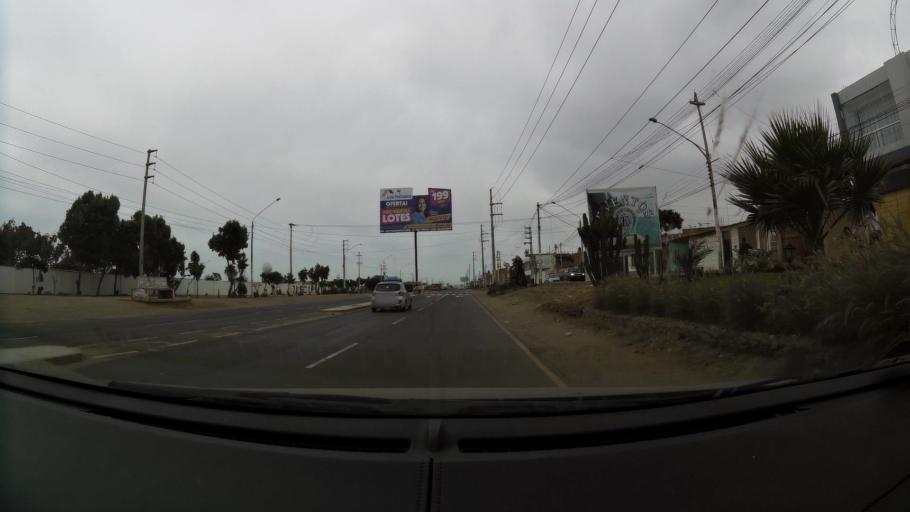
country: PE
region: La Libertad
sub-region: Provincia de Trujillo
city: Huanchaco
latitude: -8.0911
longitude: -79.0847
